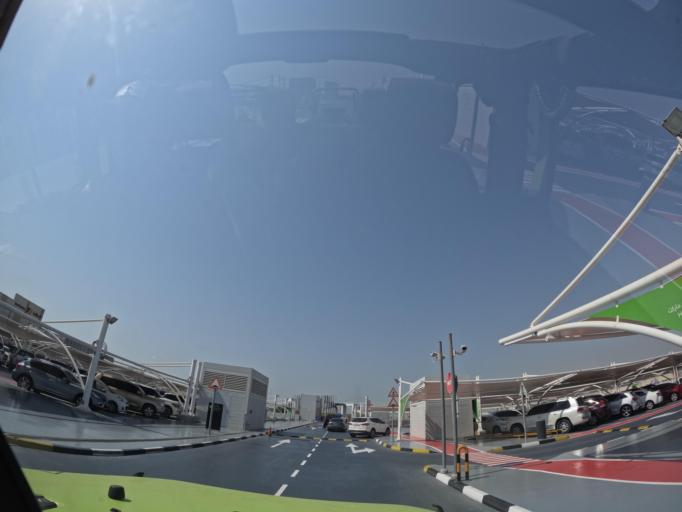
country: AE
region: Abu Dhabi
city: Abu Dhabi
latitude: 24.4897
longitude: 54.6112
